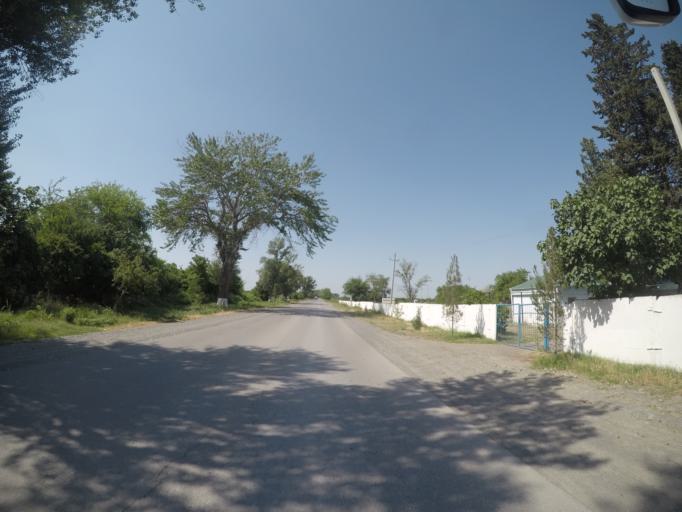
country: AZ
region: Agdas
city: Agdas
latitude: 40.6983
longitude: 47.5422
